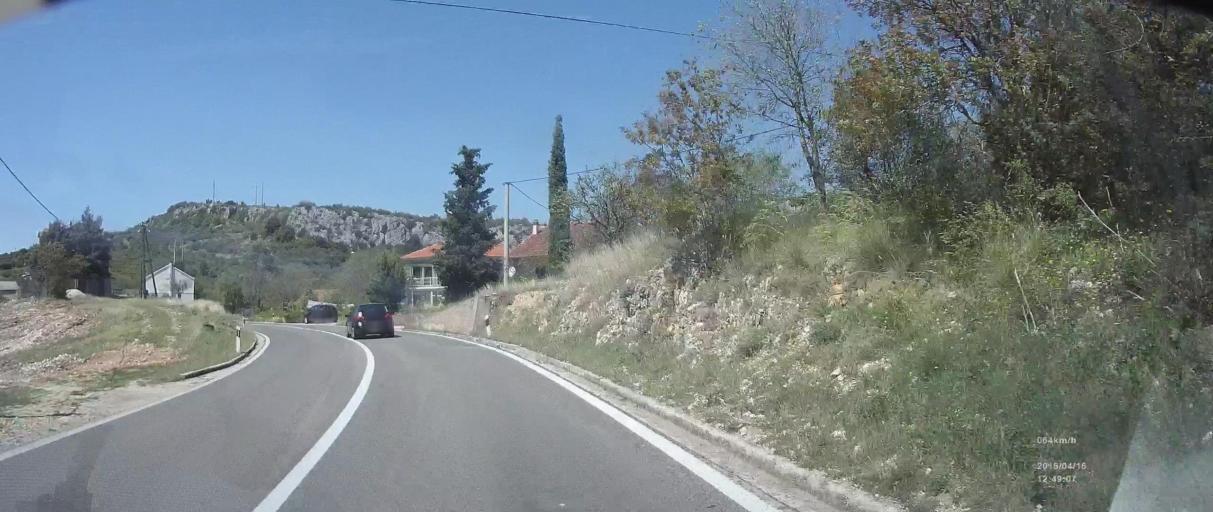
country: HR
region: Sibensko-Kniniska
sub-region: Grad Sibenik
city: Brodarica
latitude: 43.6733
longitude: 16.0296
